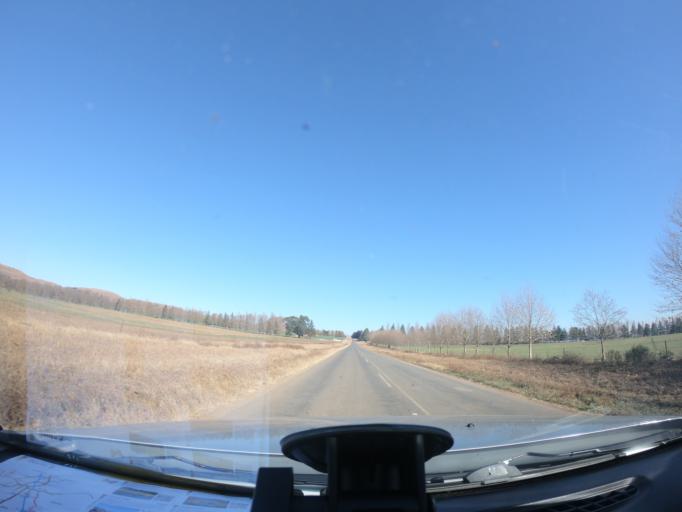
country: ZA
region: KwaZulu-Natal
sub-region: uMgungundlovu District Municipality
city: Mooirivier
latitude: -29.3255
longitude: 29.8309
